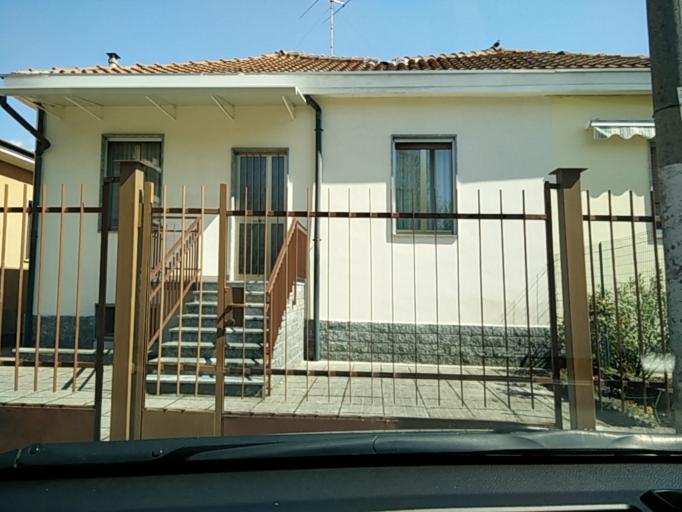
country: IT
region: Lombardy
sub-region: Provincia di Pavia
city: Valle Salimbene
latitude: 45.1767
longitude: 9.2012
